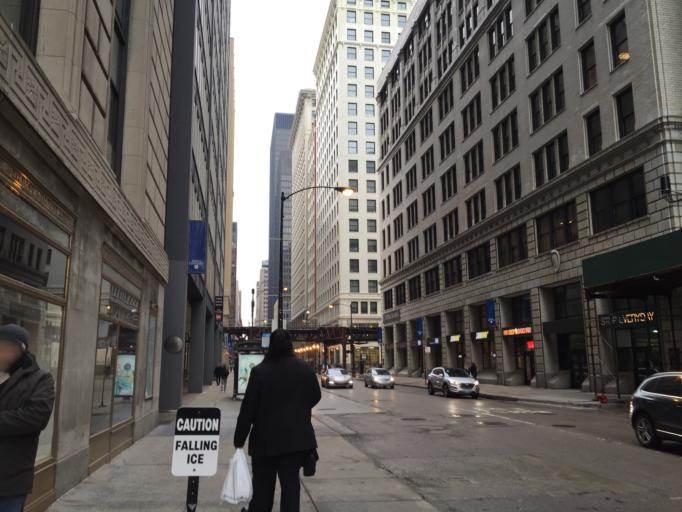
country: US
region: Illinois
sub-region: Cook County
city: Chicago
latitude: 41.8782
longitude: -87.6251
